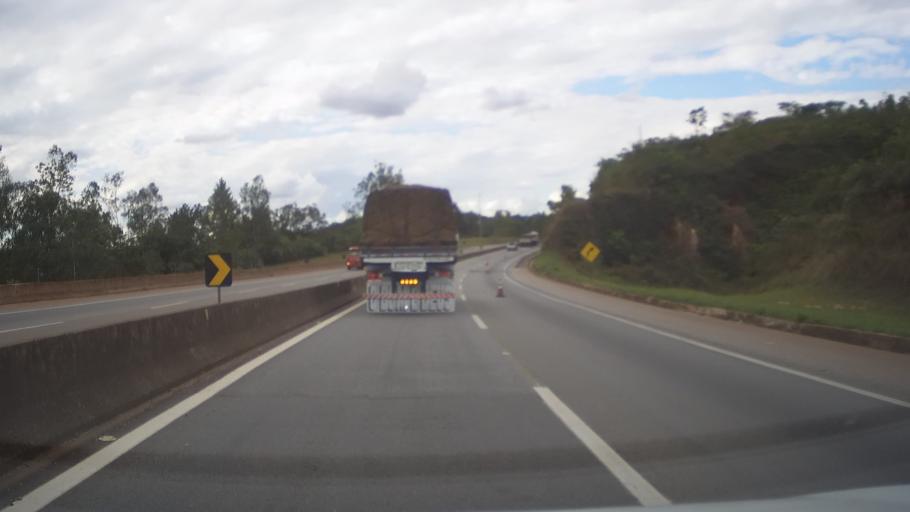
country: BR
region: Minas Gerais
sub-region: Itauna
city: Itauna
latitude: -20.3240
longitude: -44.4567
